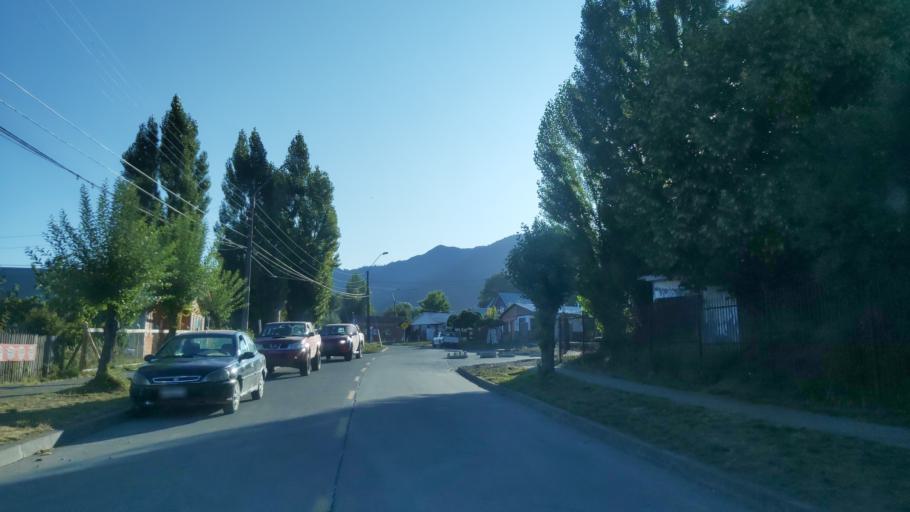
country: AR
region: Neuquen
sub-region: Departamento de Loncopue
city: Loncopue
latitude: -38.4498
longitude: -71.3703
